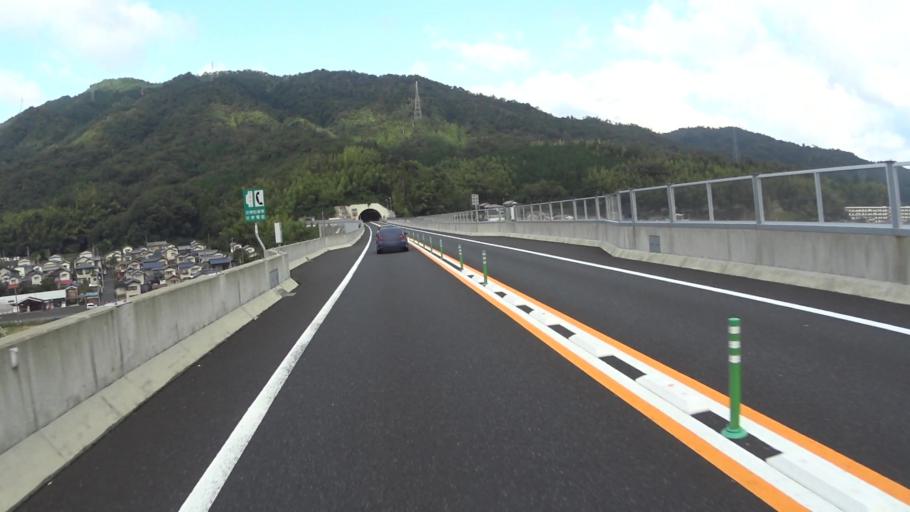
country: JP
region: Kyoto
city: Miyazu
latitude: 35.5260
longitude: 135.1767
